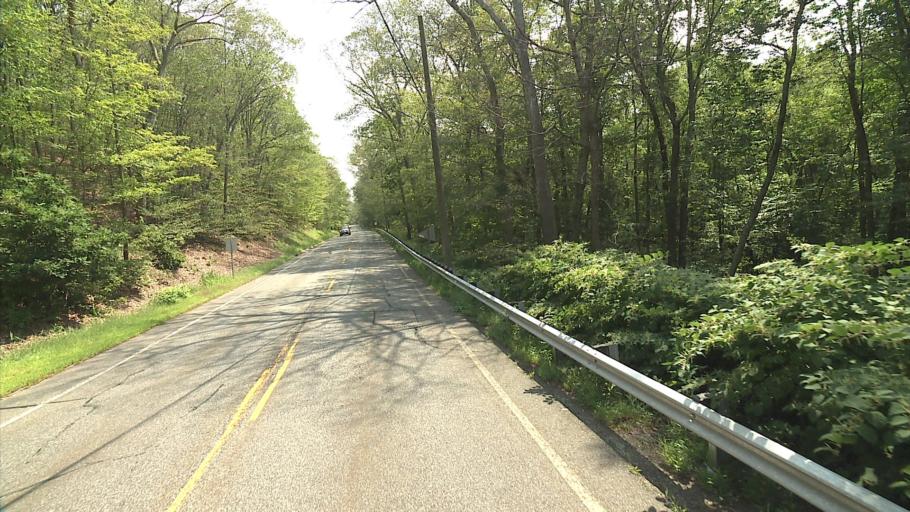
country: US
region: Connecticut
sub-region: New London County
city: Montville Center
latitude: 41.5023
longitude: -72.1794
